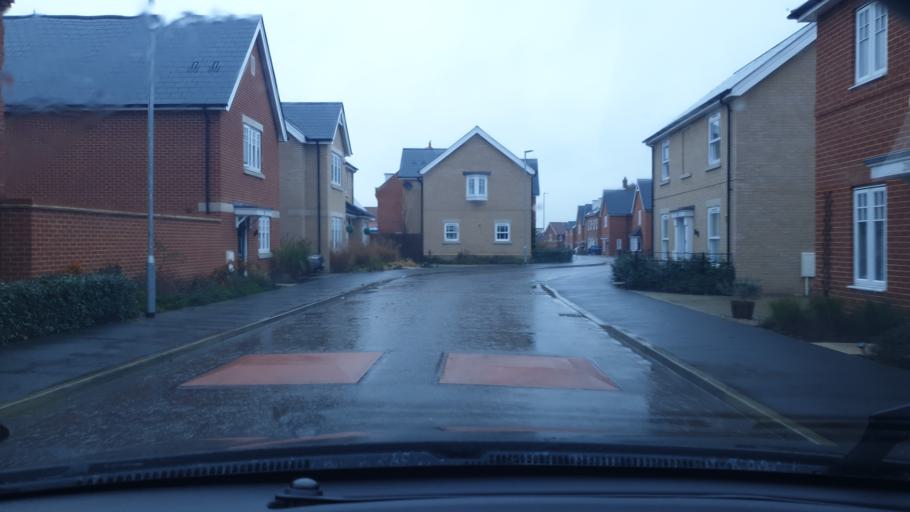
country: GB
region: England
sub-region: Essex
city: Great Horkesley
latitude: 51.9172
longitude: 0.8814
